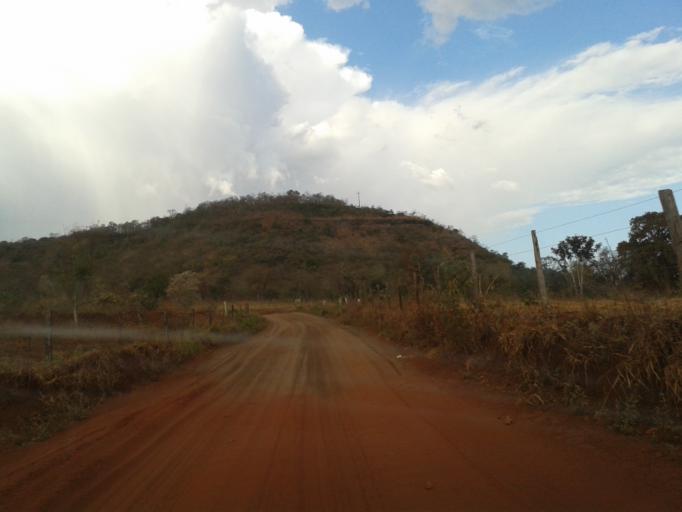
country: BR
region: Minas Gerais
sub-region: Santa Vitoria
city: Santa Vitoria
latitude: -19.2036
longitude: -49.8865
